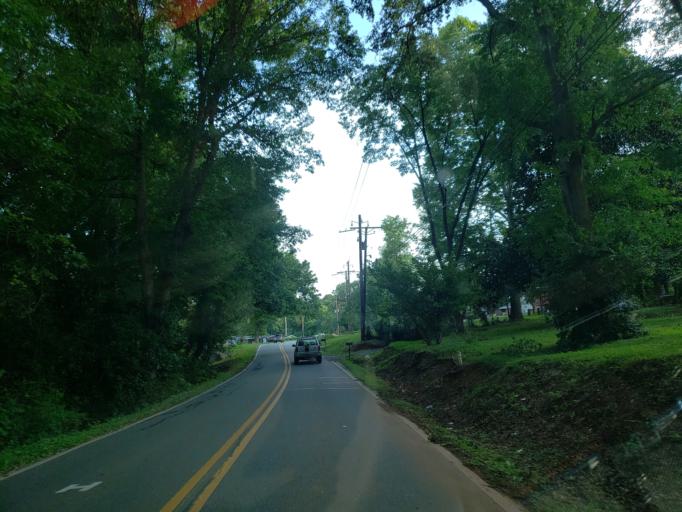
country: US
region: Georgia
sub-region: Bartow County
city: Cartersville
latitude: 34.1980
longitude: -84.8133
